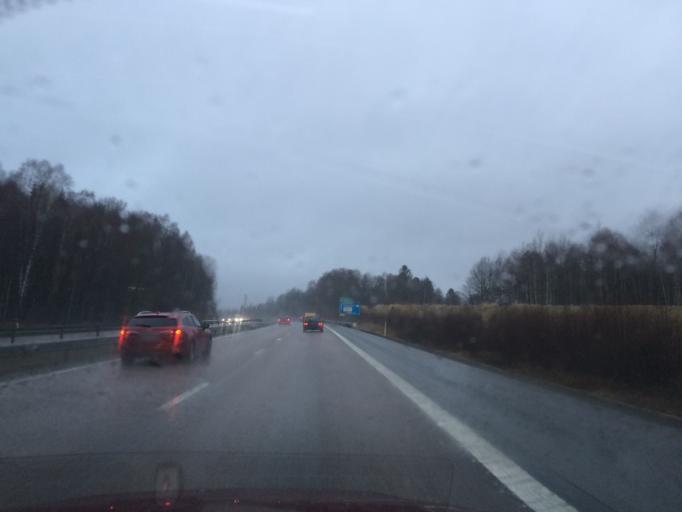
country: SE
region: Vaestra Goetaland
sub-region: Molndal
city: Lindome
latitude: 57.5842
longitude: 12.0637
